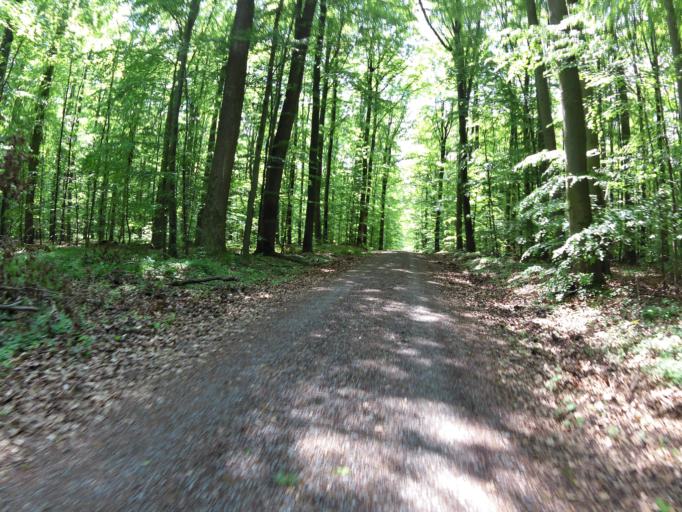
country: DE
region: Bavaria
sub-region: Regierungsbezirk Unterfranken
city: Wuerzburg
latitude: 49.7418
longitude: 9.8707
